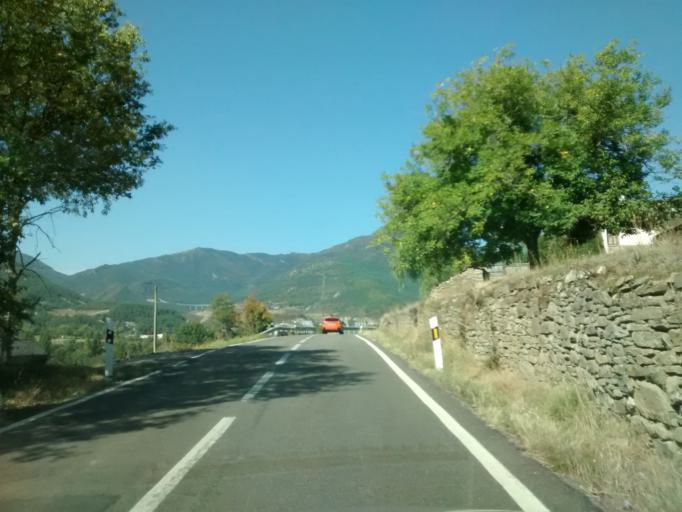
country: ES
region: Aragon
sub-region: Provincia de Huesca
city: Fiscal
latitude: 42.4907
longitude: -0.0992
